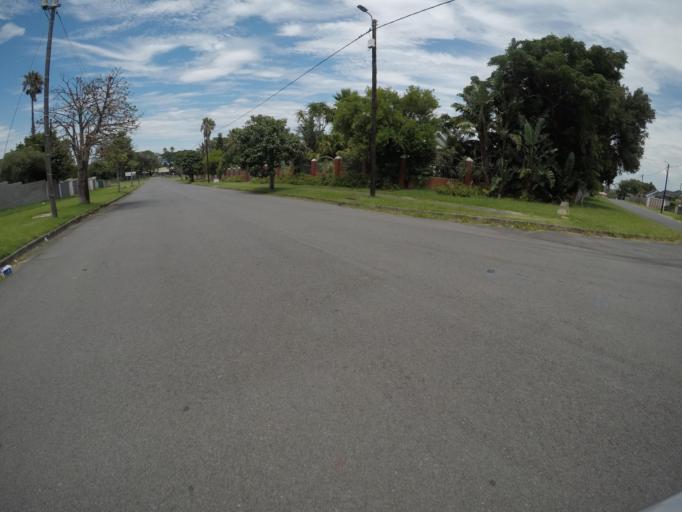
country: ZA
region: Eastern Cape
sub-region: Buffalo City Metropolitan Municipality
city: East London
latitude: -33.0415
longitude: 27.8565
